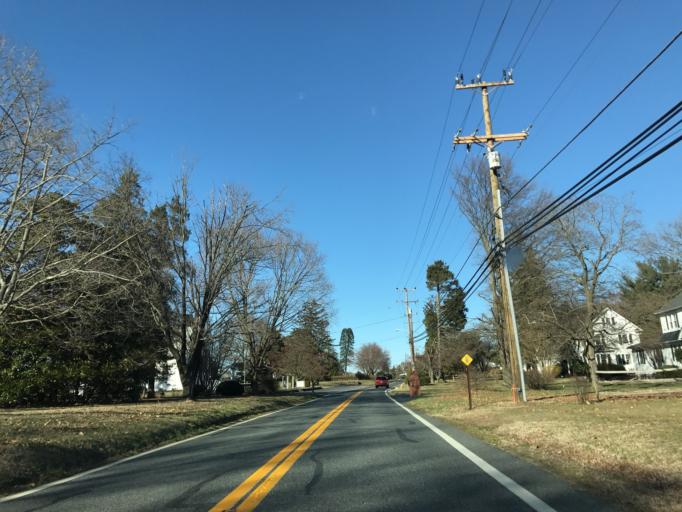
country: US
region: Maryland
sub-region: Harford County
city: Perryman
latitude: 39.4633
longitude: -76.2064
